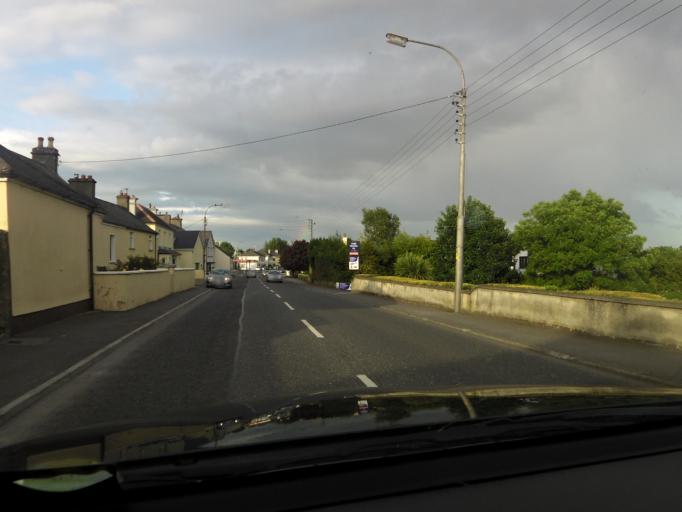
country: IE
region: Leinster
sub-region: An Iarmhi
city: Athlone
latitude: 53.4240
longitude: -7.9683
